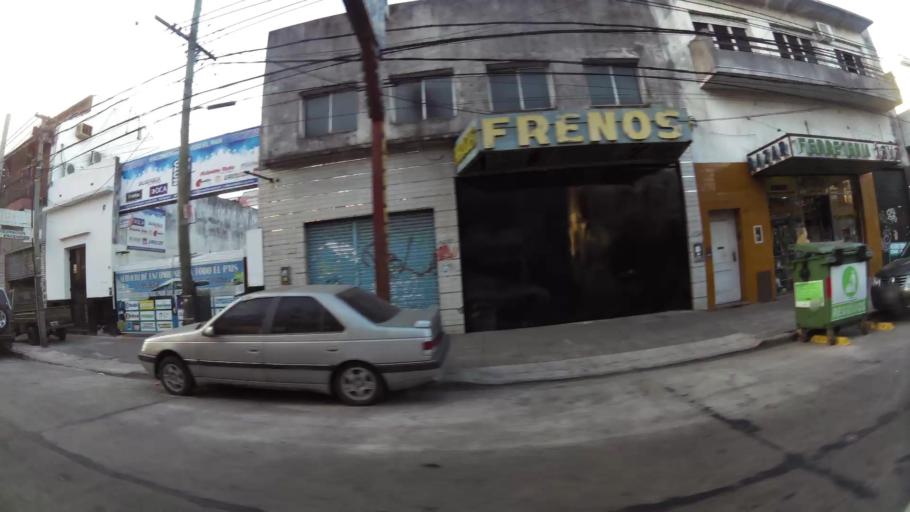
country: AR
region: Buenos Aires
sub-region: Partido de General San Martin
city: General San Martin
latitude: -34.5463
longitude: -58.5006
